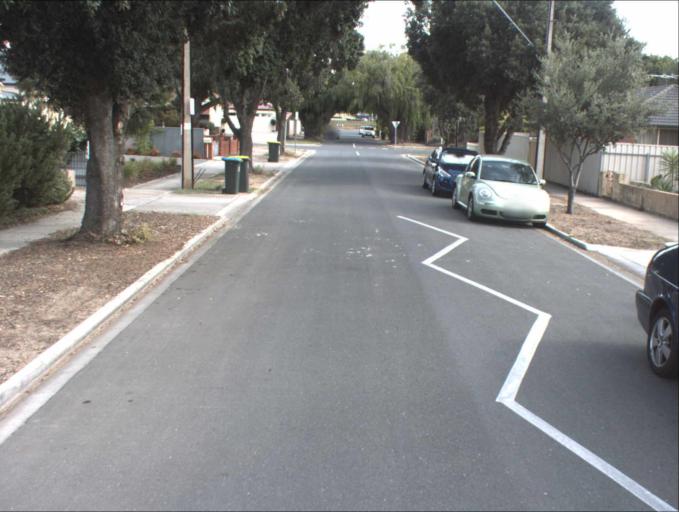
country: AU
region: South Australia
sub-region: Port Adelaide Enfield
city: Birkenhead
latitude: -34.8229
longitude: 138.4936
